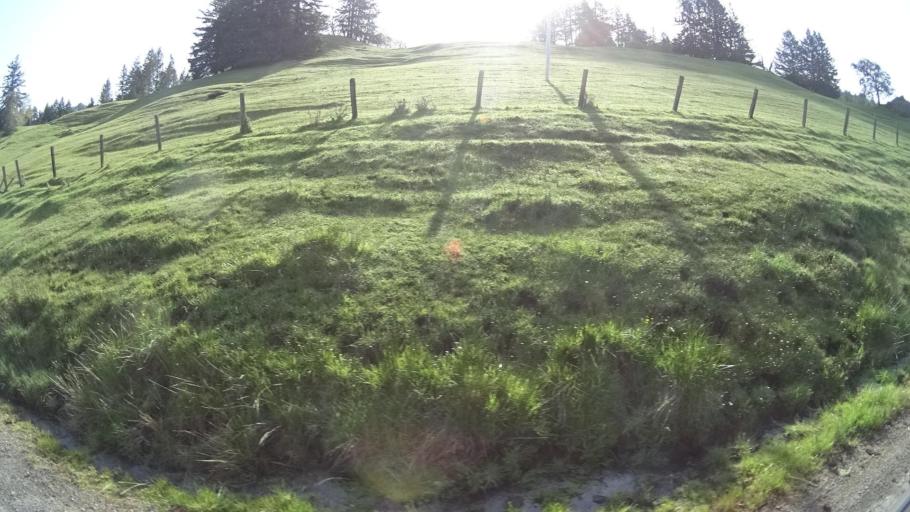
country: US
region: California
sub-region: Humboldt County
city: Bayside
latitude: 40.6889
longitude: -123.9382
